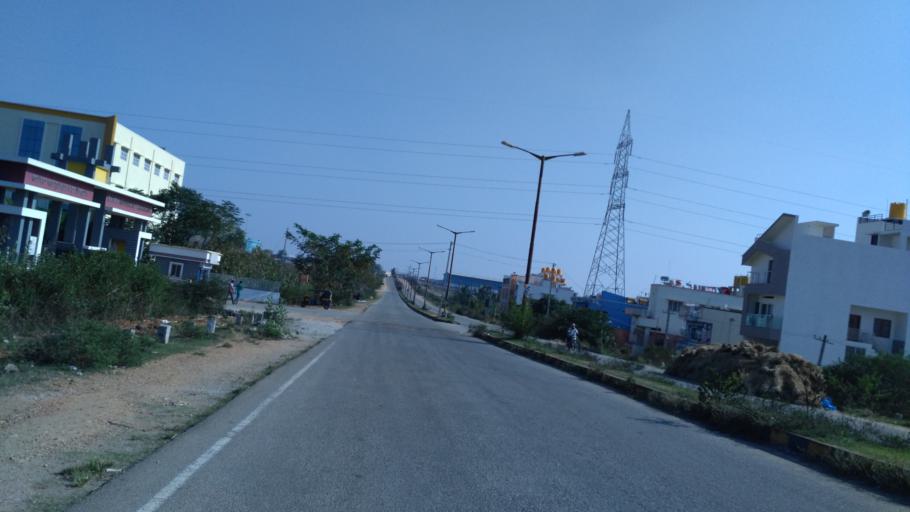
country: IN
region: Karnataka
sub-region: Hassan
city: Hassan
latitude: 12.9896
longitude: 76.1139
